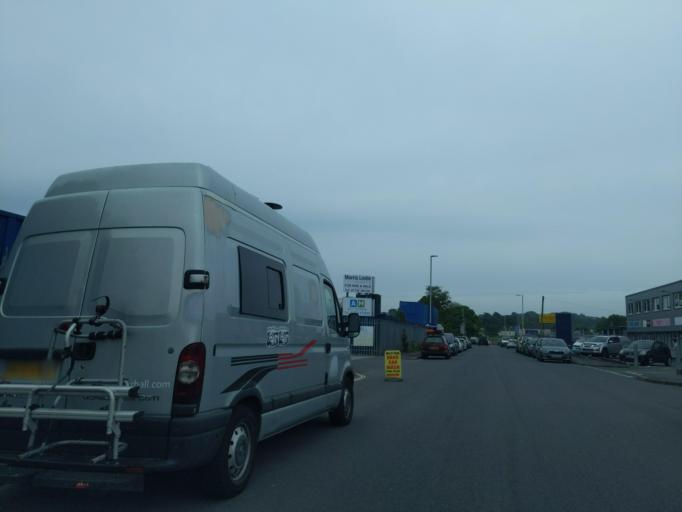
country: GB
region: England
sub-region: Devon
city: Plympton
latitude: 50.3884
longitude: -4.0675
